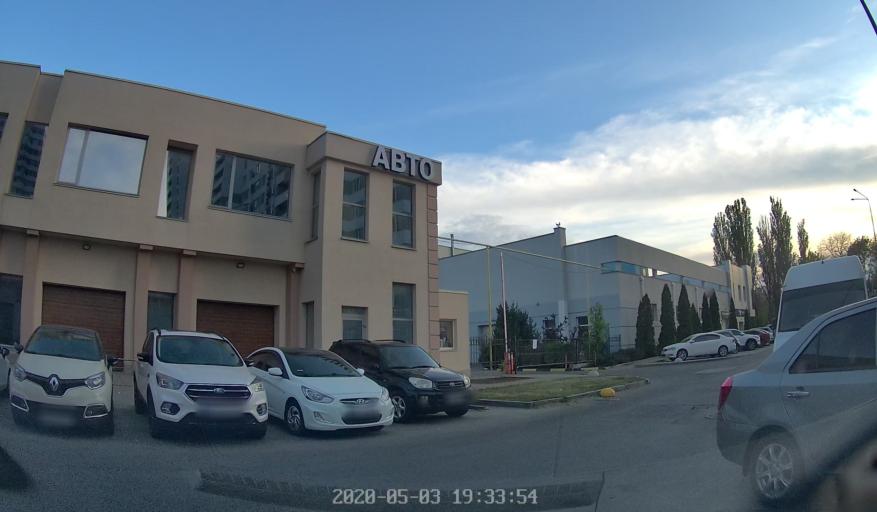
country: TR
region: Kirklareli
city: Sergen
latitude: 41.7796
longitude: 27.6538
